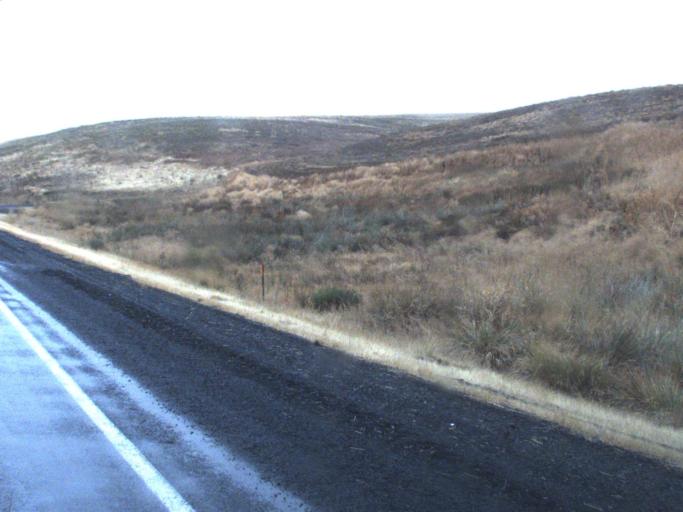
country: US
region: Washington
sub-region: Whitman County
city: Colfax
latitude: 47.1158
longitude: -117.6646
